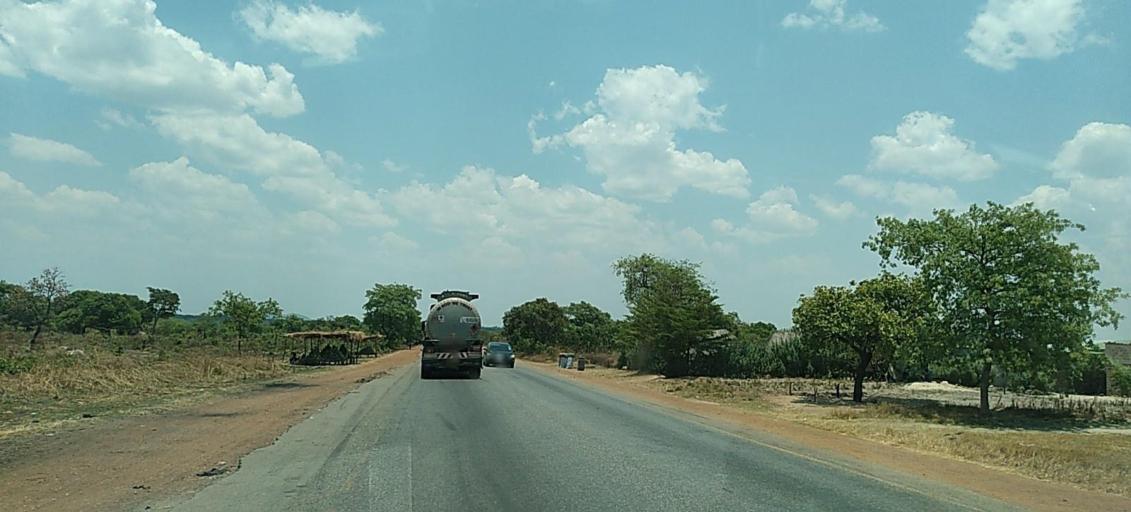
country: ZM
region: Central
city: Kapiri Mposhi
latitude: -13.7741
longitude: 28.6448
